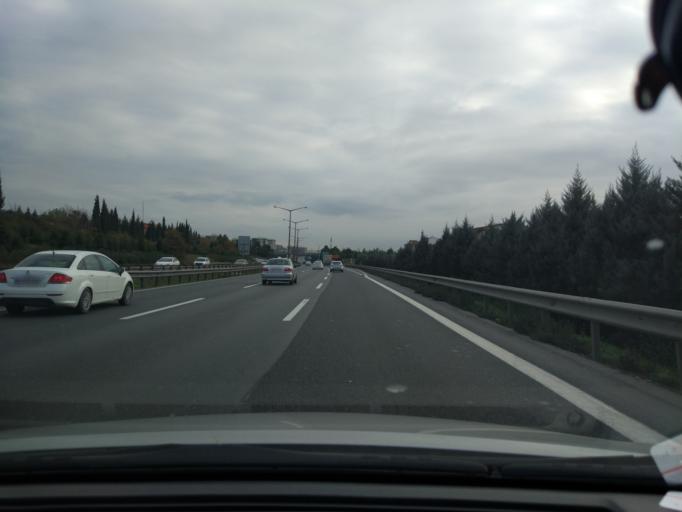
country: TR
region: Kocaeli
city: Korfez
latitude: 40.7705
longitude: 29.7803
